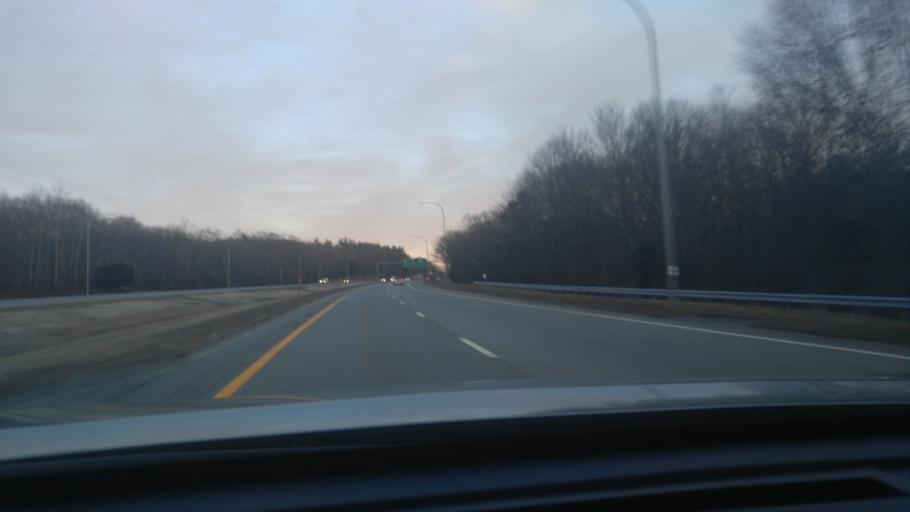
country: US
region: Rhode Island
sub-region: Washington County
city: North Kingstown
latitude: 41.5310
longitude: -71.4592
